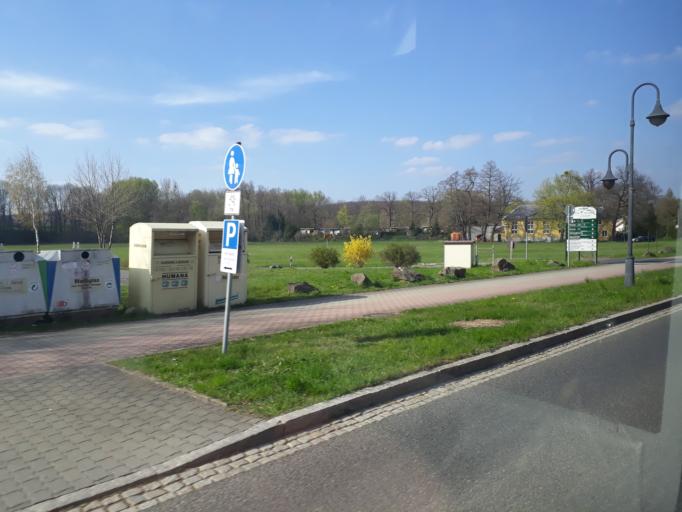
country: DE
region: Saxony
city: Kreischa
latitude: 50.9491
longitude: 13.7671
